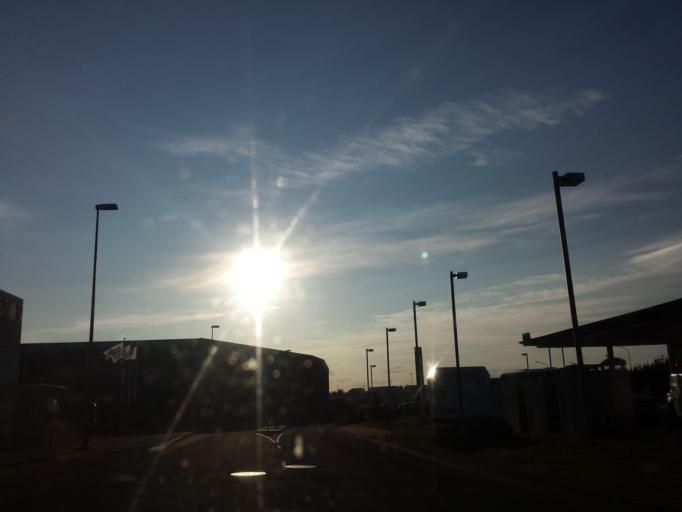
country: IS
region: Capital Region
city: Mosfellsbaer
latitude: 64.1026
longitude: -21.7663
